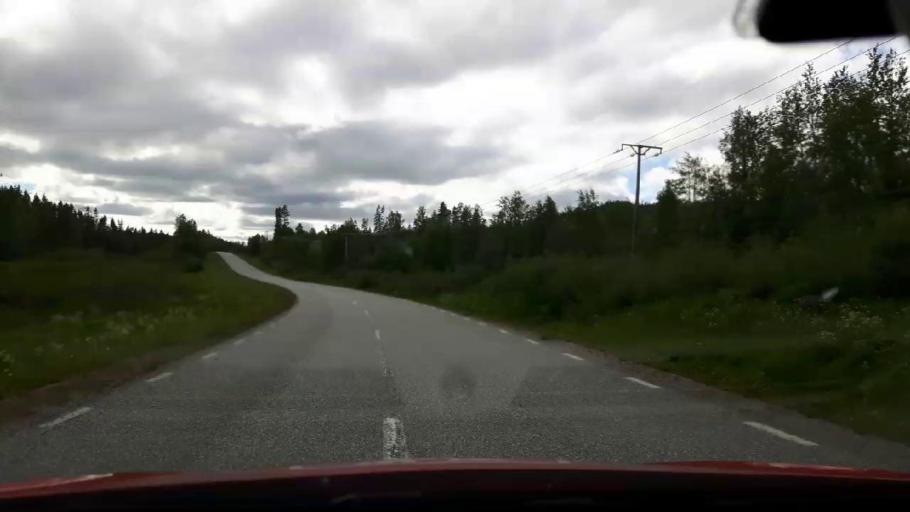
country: SE
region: Jaemtland
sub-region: Ragunda Kommun
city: Hammarstrand
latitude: 62.9660
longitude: 16.0098
